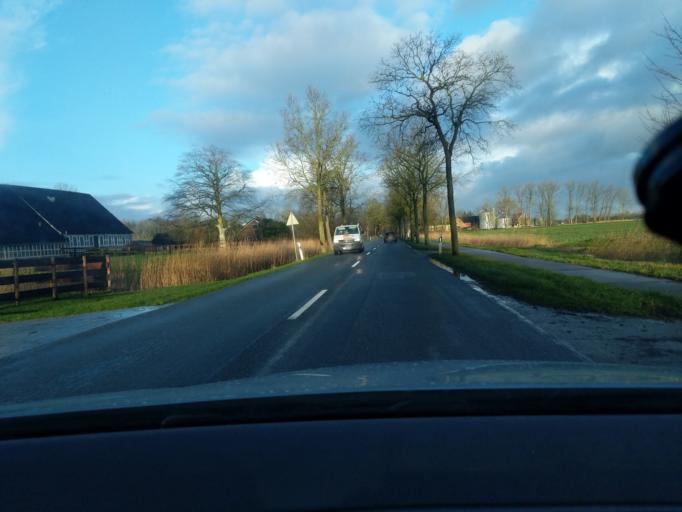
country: DE
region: Lower Saxony
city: Cuxhaven
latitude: 53.8237
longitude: 8.7466
